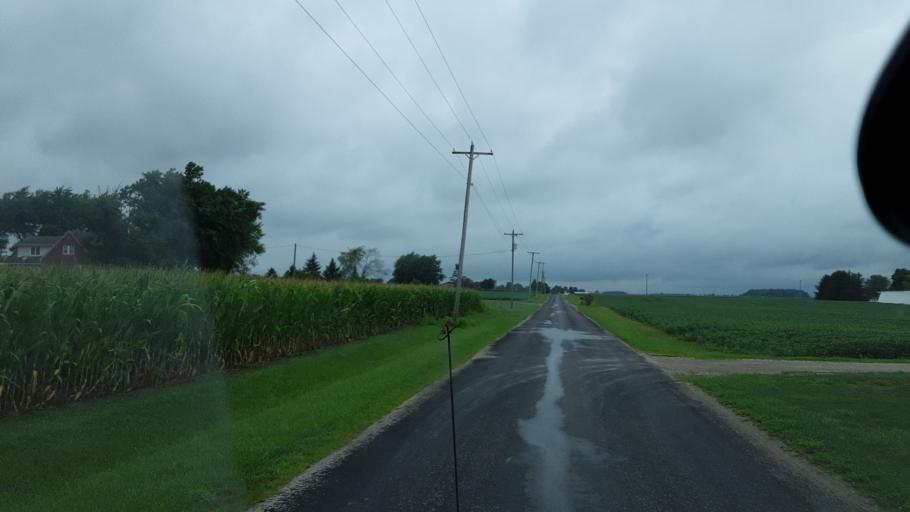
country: US
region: Indiana
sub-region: Allen County
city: Monroeville
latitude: 40.8884
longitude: -84.8423
